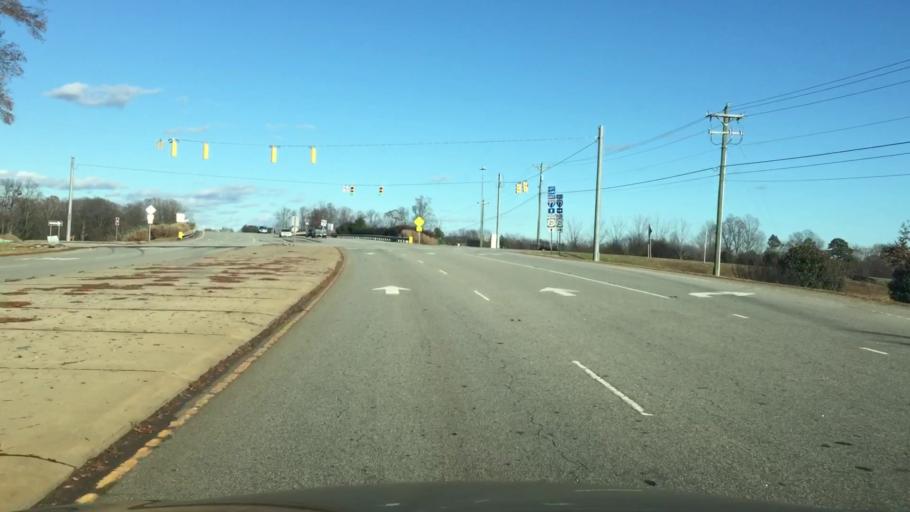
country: US
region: North Carolina
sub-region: Gaston County
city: Davidson
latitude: 35.5293
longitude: -80.8649
